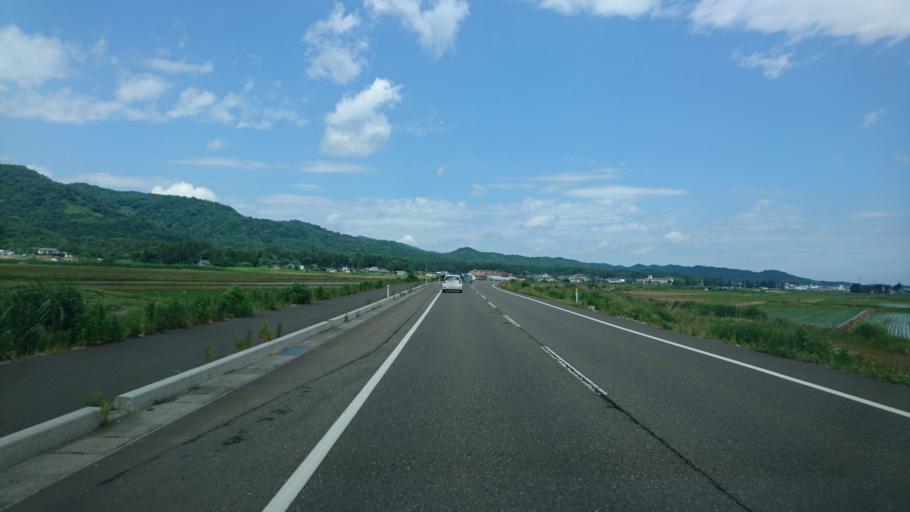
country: JP
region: Niigata
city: Arai
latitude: 37.0719
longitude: 138.2370
